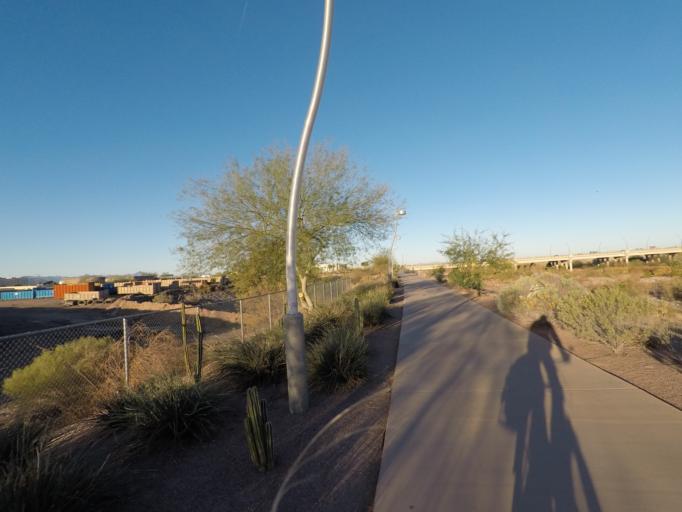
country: US
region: Arizona
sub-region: Maricopa County
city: Tempe Junction
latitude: 33.4335
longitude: -111.9584
